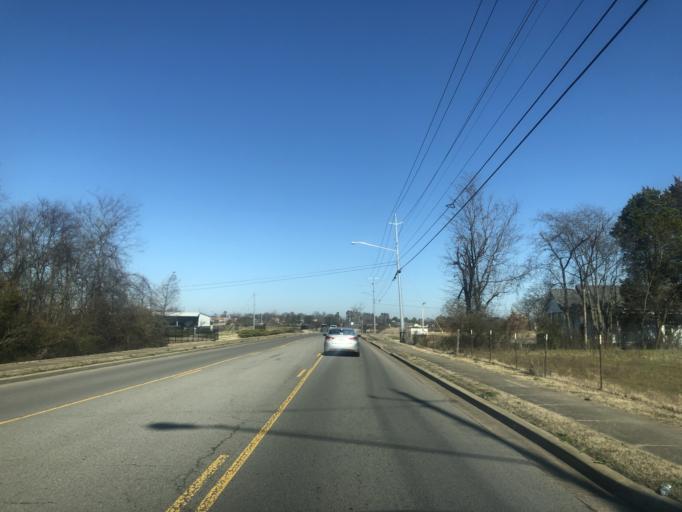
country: US
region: Tennessee
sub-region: Rutherford County
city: Smyrna
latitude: 35.9176
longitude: -86.4685
